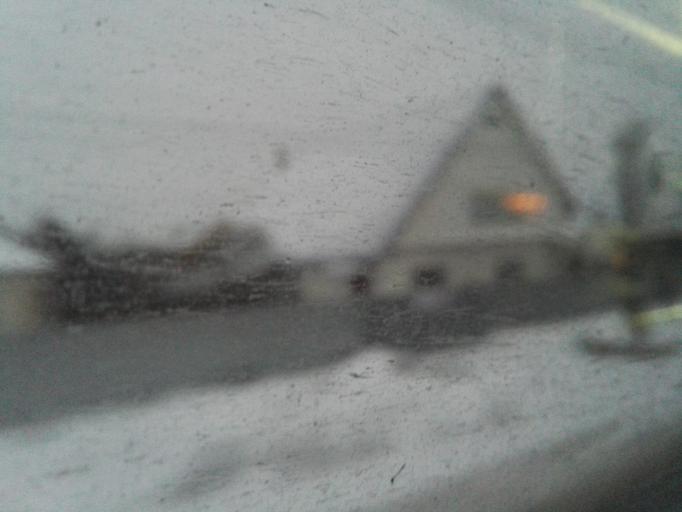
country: RU
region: Tula
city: Tula
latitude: 54.1670
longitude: 37.6057
